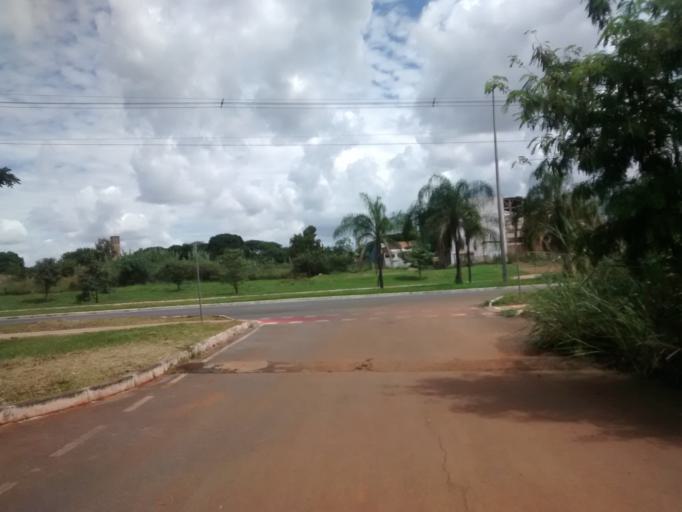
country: BR
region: Federal District
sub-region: Brasilia
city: Brasilia
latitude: -15.7542
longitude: -47.8766
